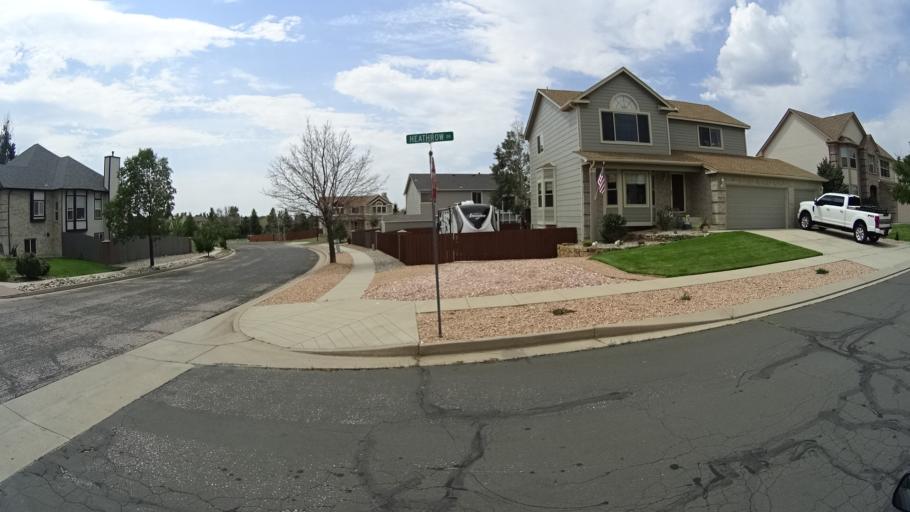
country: US
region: Colorado
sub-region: El Paso County
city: Black Forest
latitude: 38.9624
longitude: -104.7772
